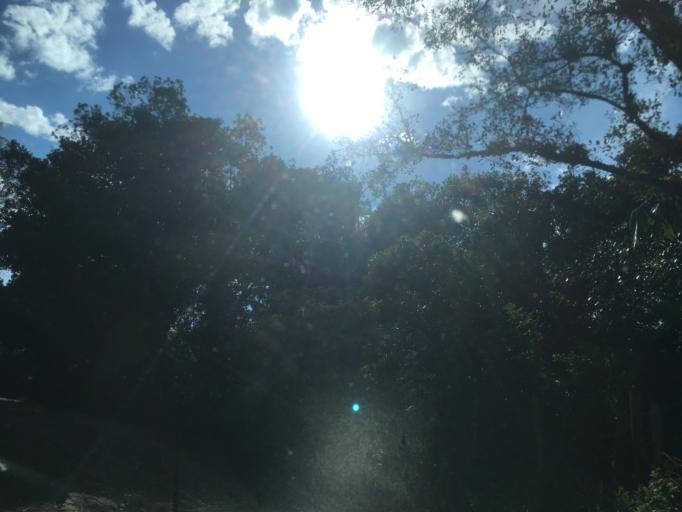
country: CO
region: Santander
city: Oiba
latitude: 6.1394
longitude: -73.1925
